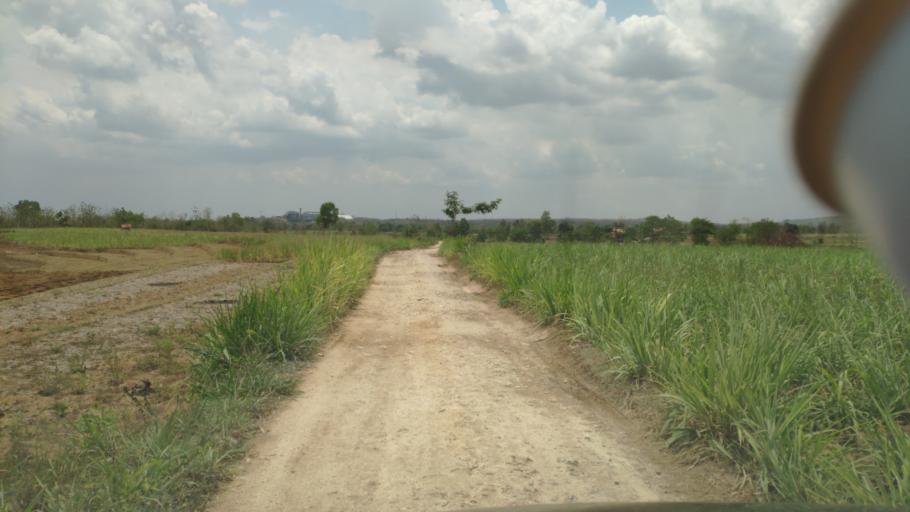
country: ID
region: Central Java
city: Ngapus
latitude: -6.9693
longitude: 111.2153
